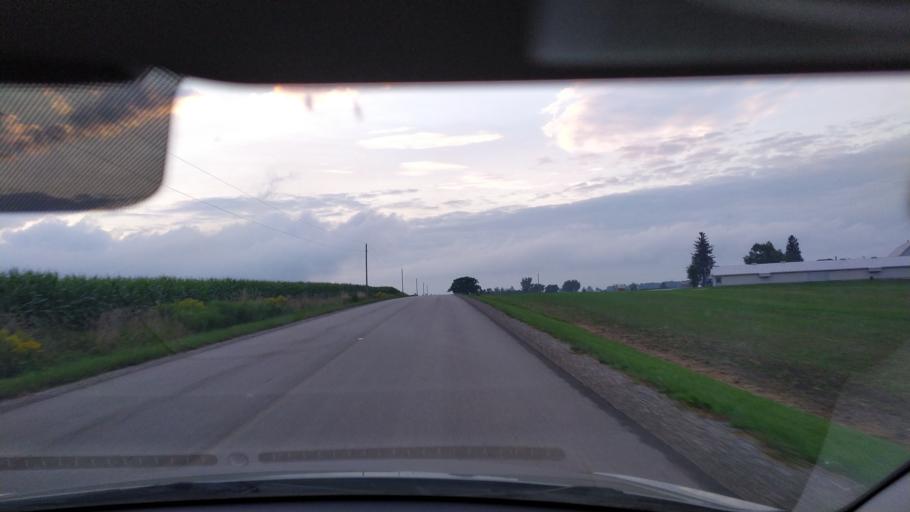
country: CA
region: Ontario
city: Kitchener
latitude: 43.3363
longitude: -80.6275
